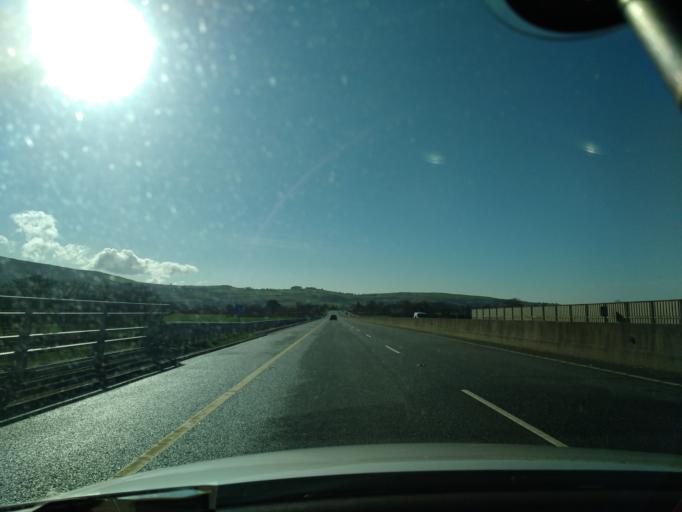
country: IE
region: Munster
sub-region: North Tipperary
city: Nenagh
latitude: 52.8146
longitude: -8.3090
